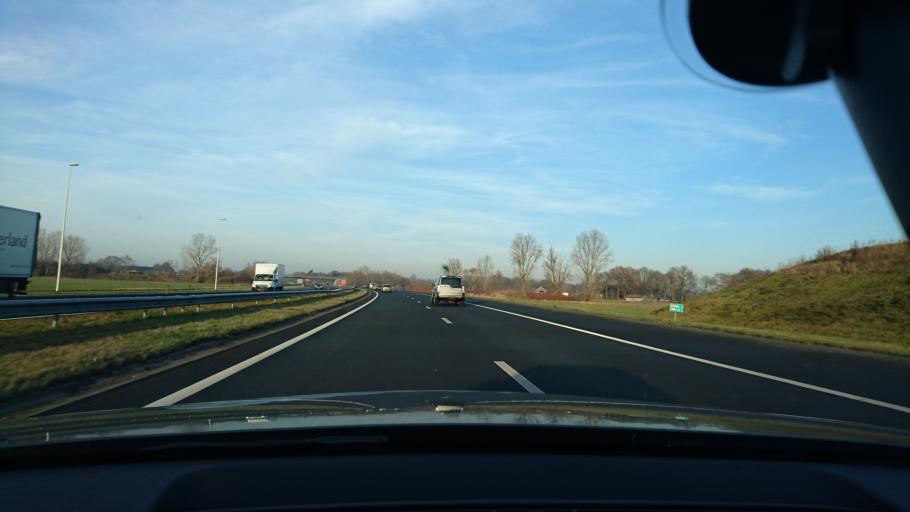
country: NL
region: North Brabant
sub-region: Gemeente Son en Breugel
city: Son
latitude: 51.5369
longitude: 5.4814
